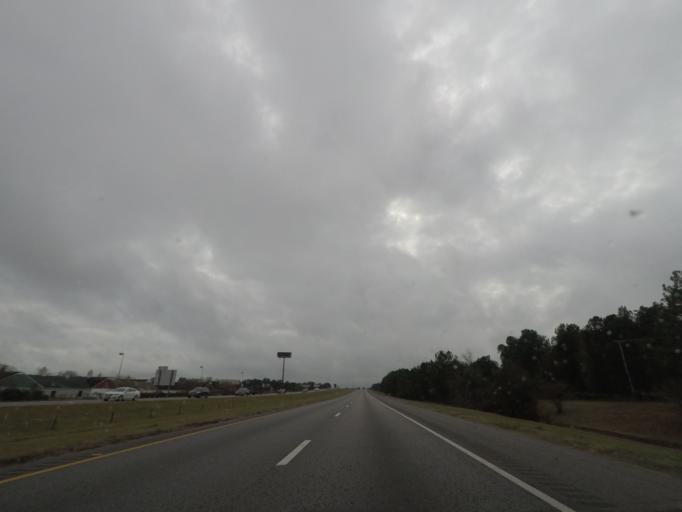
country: US
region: South Carolina
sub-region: Orangeburg County
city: Holly Hill
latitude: 33.4786
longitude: -80.4739
